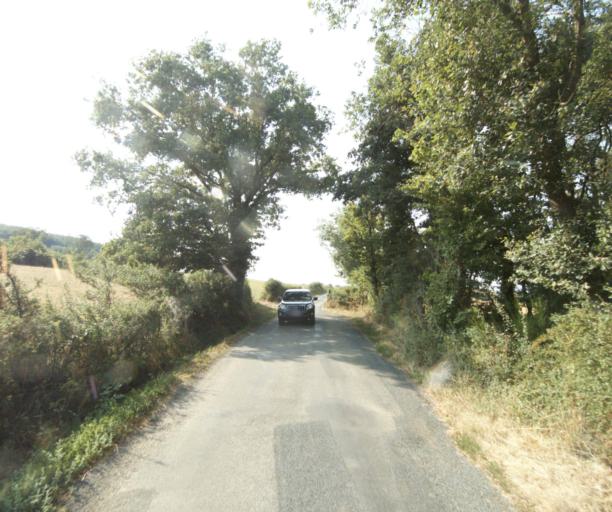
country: FR
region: Rhone-Alpes
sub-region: Departement du Rhone
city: Savigny
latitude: 45.8342
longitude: 4.5737
